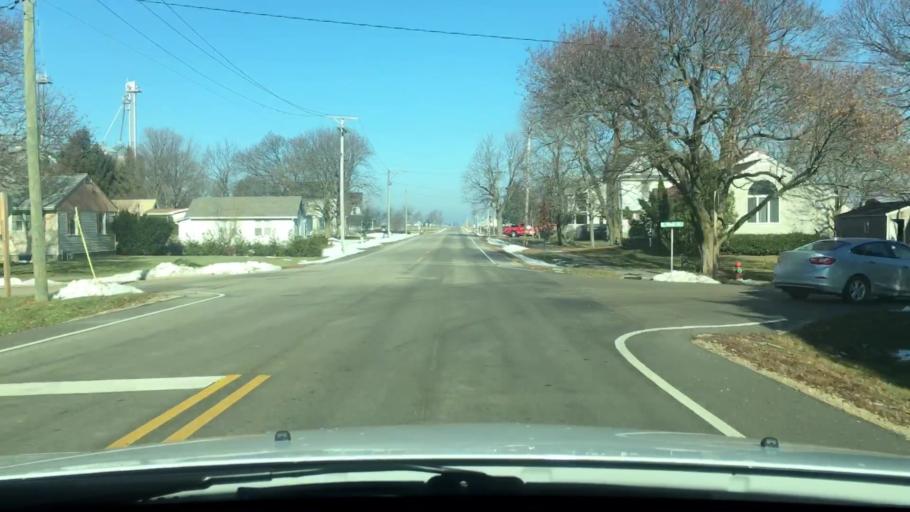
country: US
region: Illinois
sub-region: DeKalb County
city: Waterman
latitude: 41.7689
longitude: -88.8771
